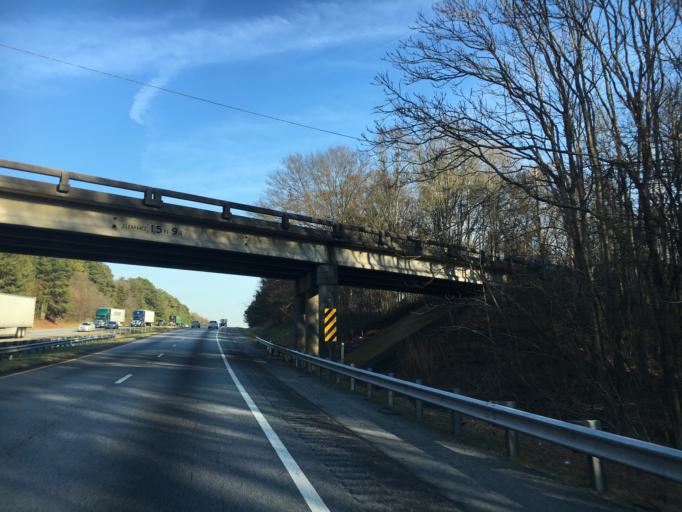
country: US
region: Georgia
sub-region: Hart County
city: Reed Creek
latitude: 34.5104
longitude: -82.9467
